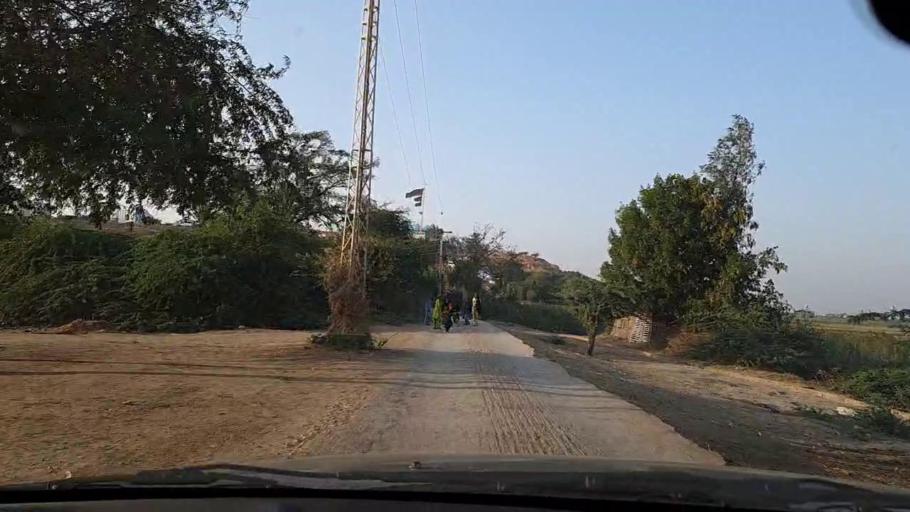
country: PK
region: Sindh
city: Thatta
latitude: 24.5597
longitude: 67.8806
